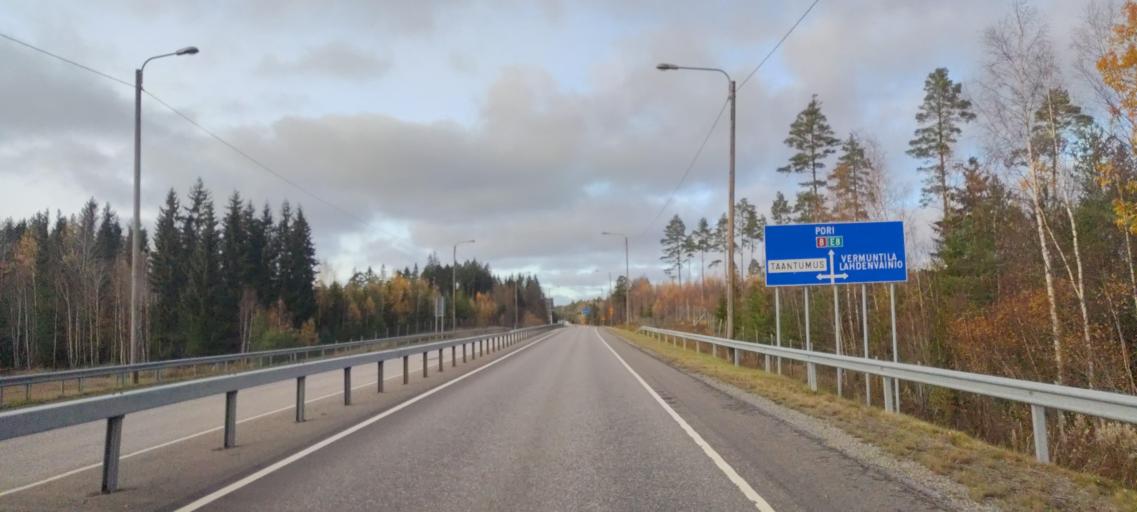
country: FI
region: Satakunta
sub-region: Rauma
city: Rauma
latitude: 61.0336
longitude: 21.5437
